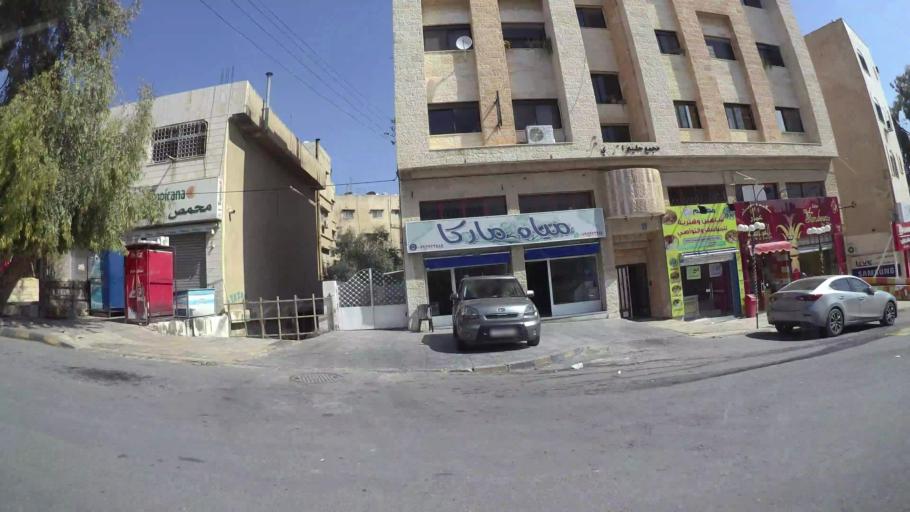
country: JO
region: Amman
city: Amman
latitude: 31.9792
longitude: 35.9865
